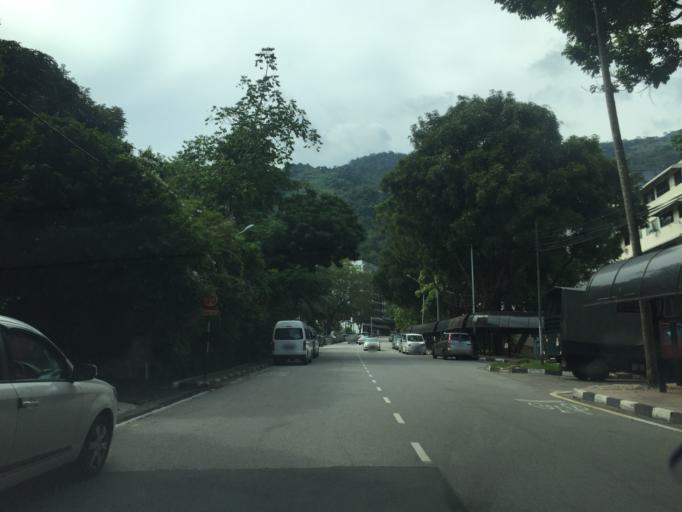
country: MY
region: Penang
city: George Town
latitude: 5.4070
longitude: 100.2794
